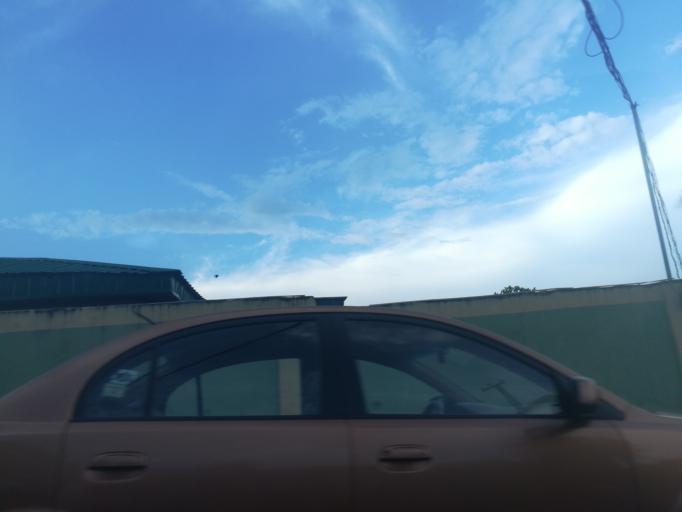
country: NG
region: Lagos
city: Ojota
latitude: 6.5632
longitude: 3.3773
